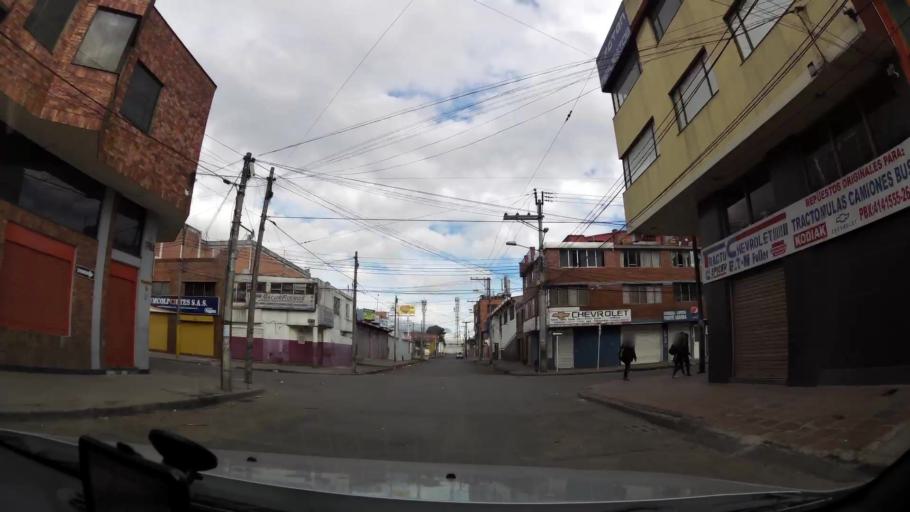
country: CO
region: Bogota D.C.
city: Bogota
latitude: 4.6308
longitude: -74.1096
